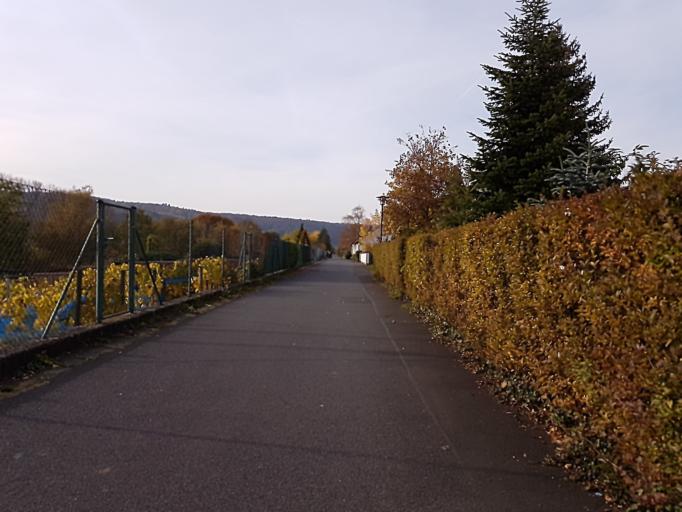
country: DE
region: Bavaria
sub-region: Regierungsbezirk Unterfranken
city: Worth am Main
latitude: 49.8024
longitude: 9.1531
